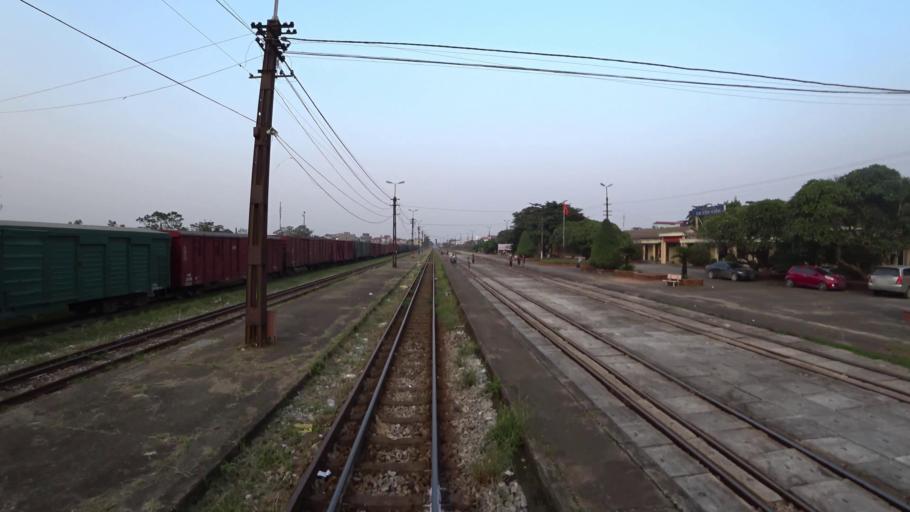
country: VN
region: Ha Noi
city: Dong Anh
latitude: 21.0974
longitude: 105.9094
